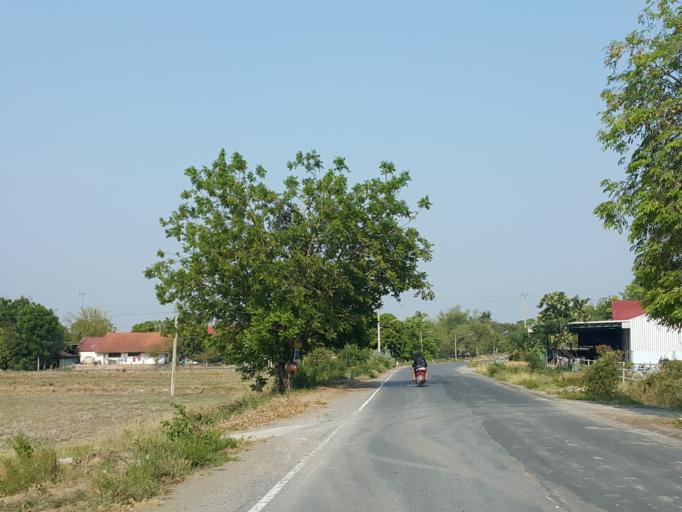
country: TH
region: Suphan Buri
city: Sam Chuk
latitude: 14.7455
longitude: 100.0290
